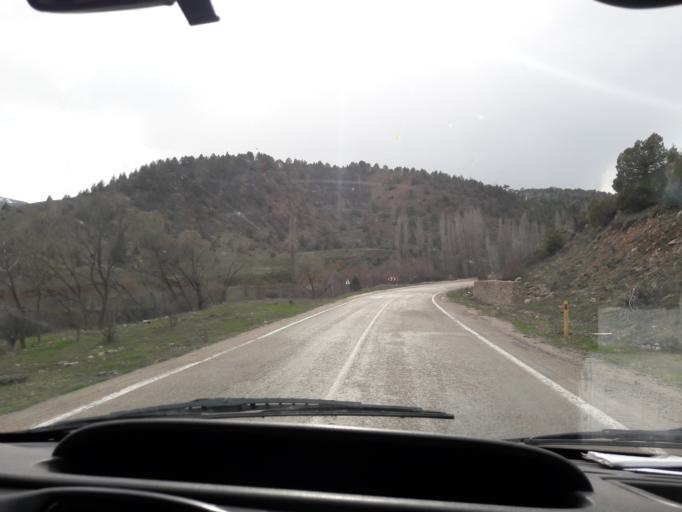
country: TR
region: Giresun
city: Alucra
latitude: 40.2658
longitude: 38.8876
